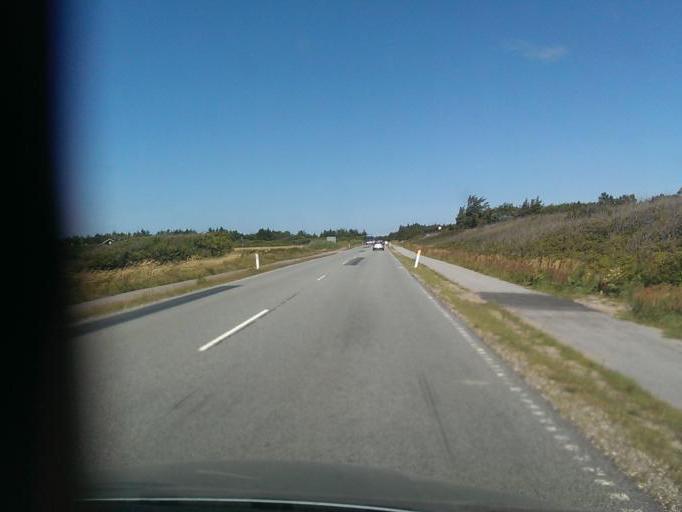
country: DK
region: North Denmark
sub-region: Jammerbugt Kommune
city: Pandrup
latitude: 57.3534
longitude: 9.7071
